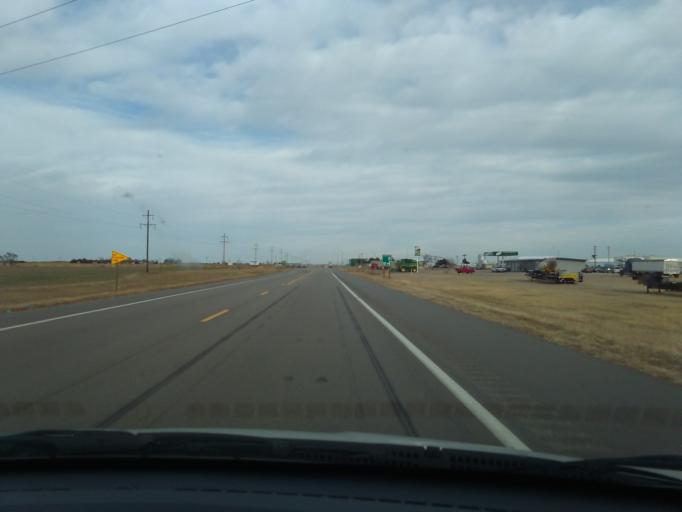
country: US
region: Nebraska
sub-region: Dundy County
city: Benkelman
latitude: 40.0589
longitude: -101.5358
